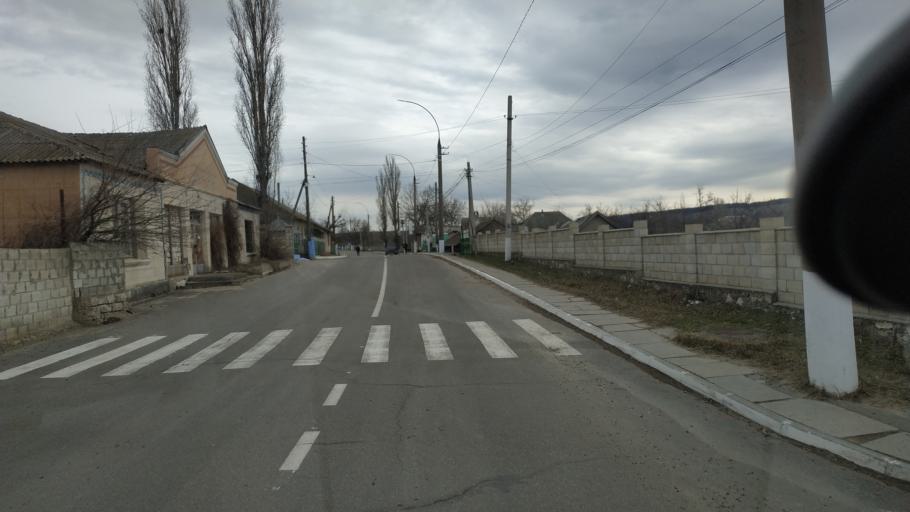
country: MD
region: Telenesti
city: Cocieri
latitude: 47.3447
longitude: 29.1133
